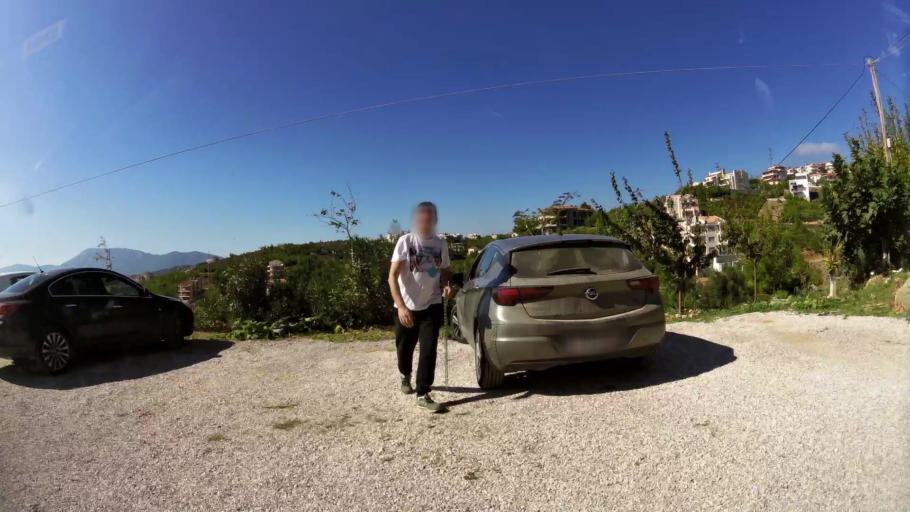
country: GR
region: Attica
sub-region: Nomarchia Anatolikis Attikis
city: Dioni
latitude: 38.0317
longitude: 23.9348
